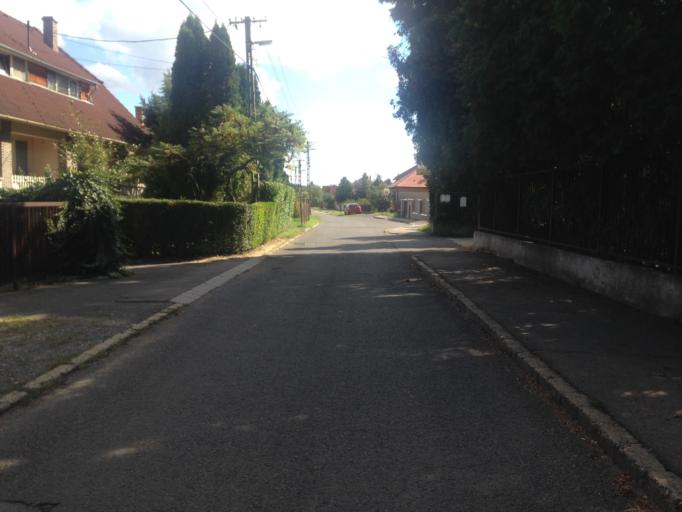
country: HU
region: Somogy
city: Kaposvar
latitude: 46.3443
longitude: 17.8090
